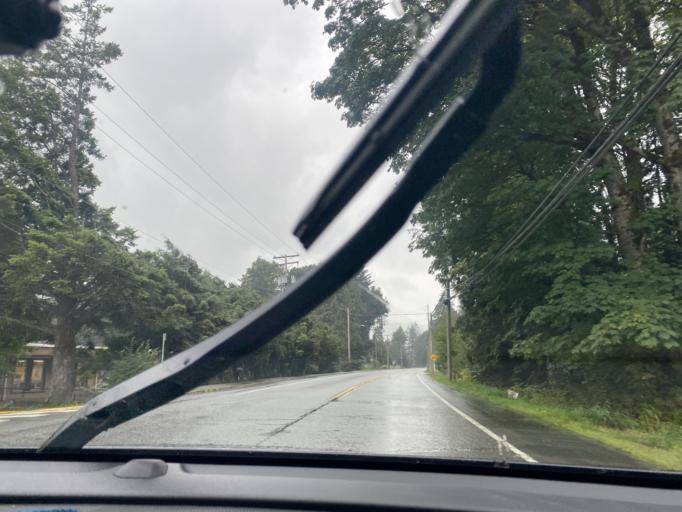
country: CA
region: British Columbia
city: Agassiz
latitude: 49.2988
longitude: -121.7850
